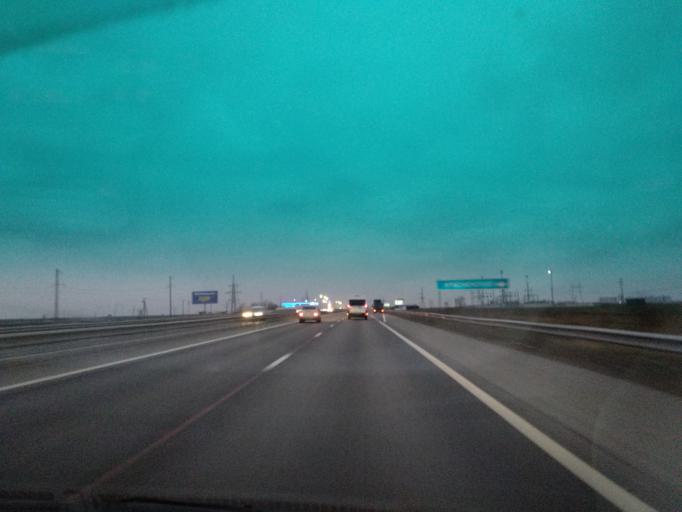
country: RU
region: Adygeya
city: Adygeysk
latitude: 44.8614
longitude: 39.1946
